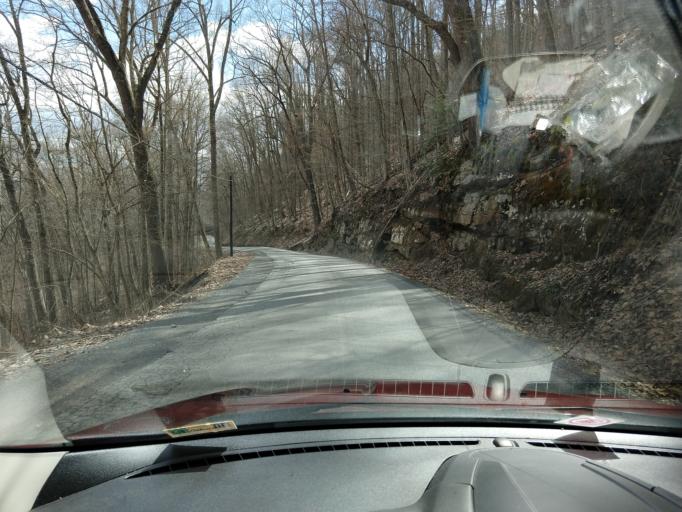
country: US
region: West Virginia
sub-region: Greenbrier County
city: Fairlea
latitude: 37.8237
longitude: -80.5120
